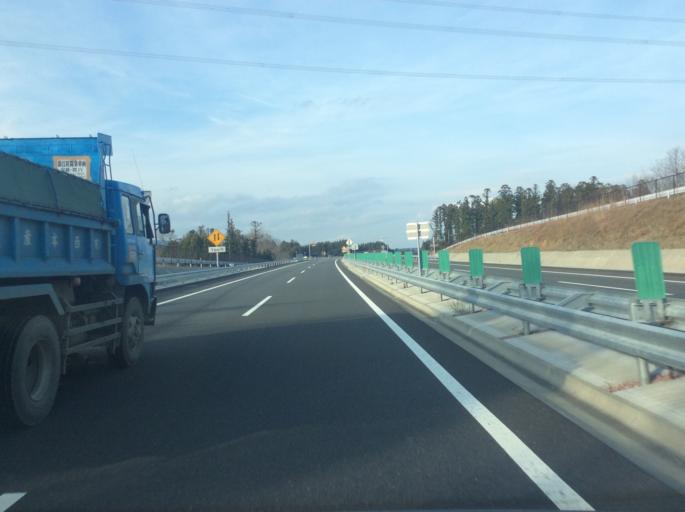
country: JP
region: Fukushima
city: Namie
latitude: 37.5291
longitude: 140.9418
